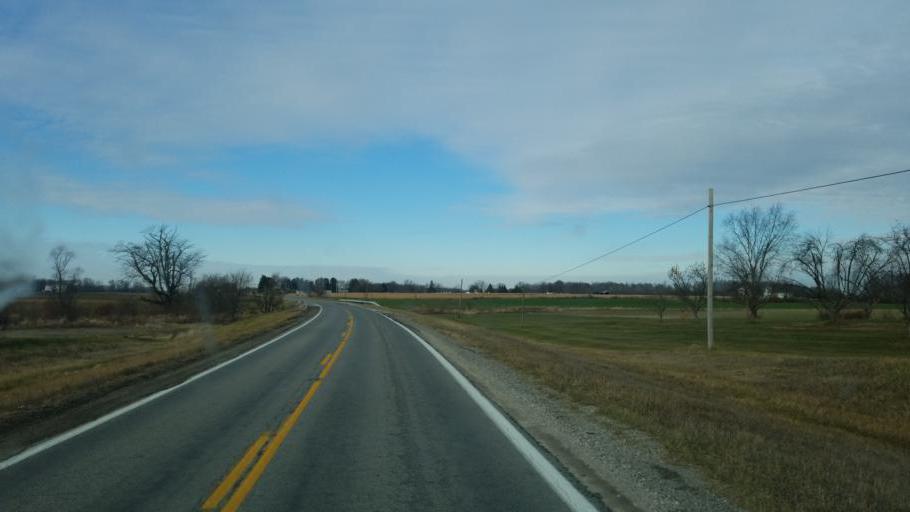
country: US
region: Ohio
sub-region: Marion County
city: Marion
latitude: 40.5492
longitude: -83.0396
